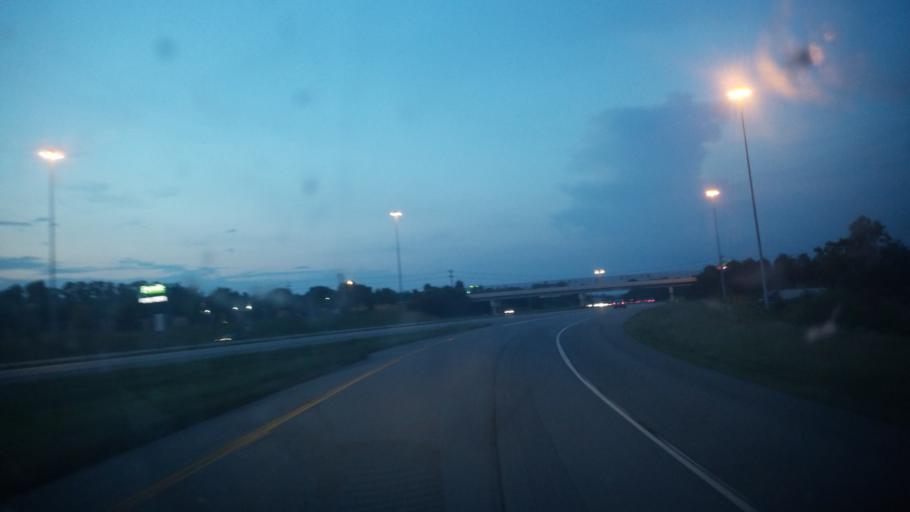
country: US
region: Ohio
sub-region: Clermont County
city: Summerside
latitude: 39.1038
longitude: -84.2820
